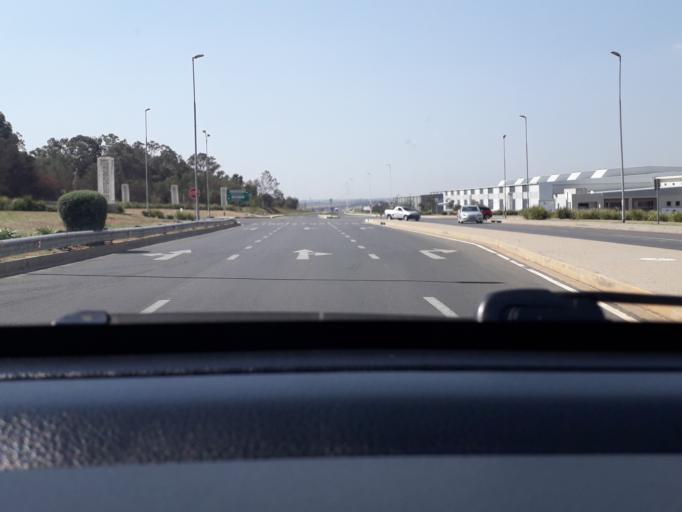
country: ZA
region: Gauteng
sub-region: City of Johannesburg Metropolitan Municipality
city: Modderfontein
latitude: -26.1006
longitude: 28.1387
